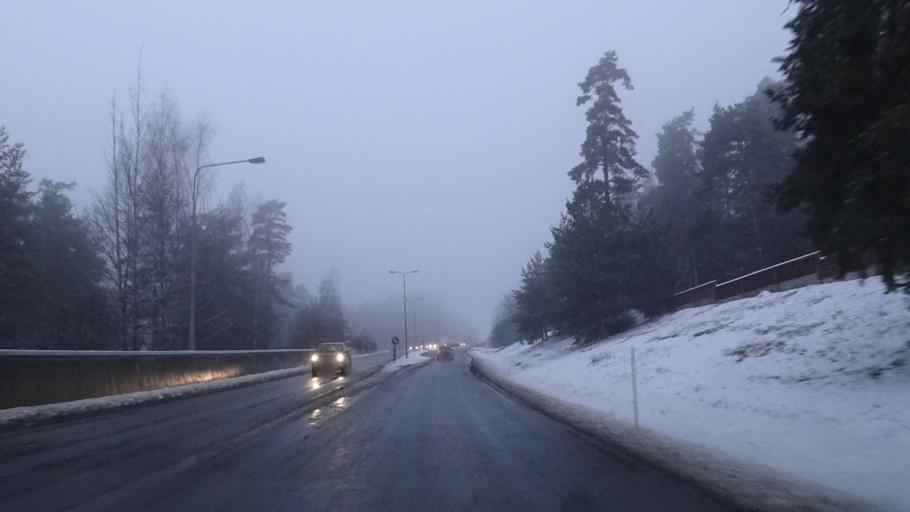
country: FI
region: Paijanne Tavastia
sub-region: Lahti
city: Hollola
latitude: 60.9834
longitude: 25.5415
